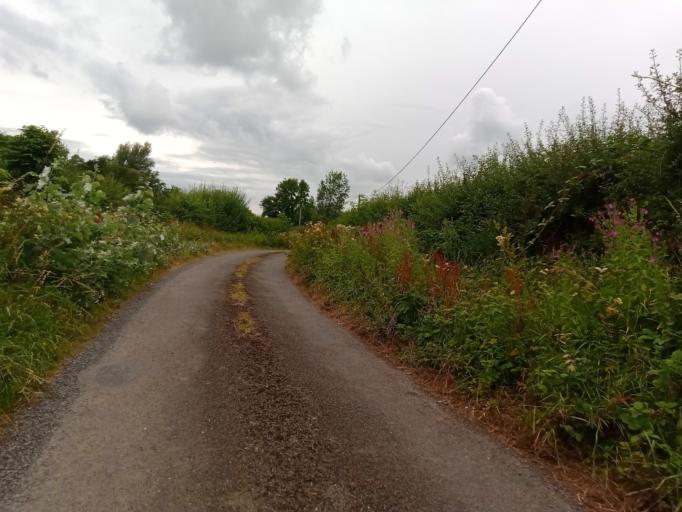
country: IE
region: Leinster
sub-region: Kilkenny
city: Callan
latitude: 52.5392
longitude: -7.4208
